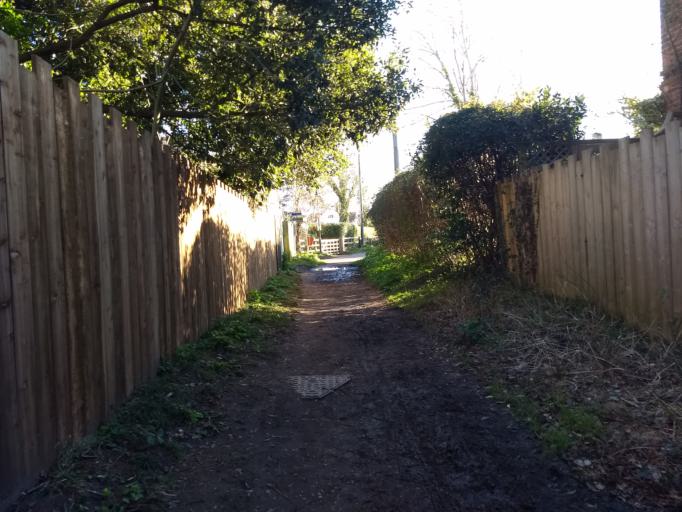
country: GB
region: England
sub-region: Isle of Wight
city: Bembridge
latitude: 50.6905
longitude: -1.0798
